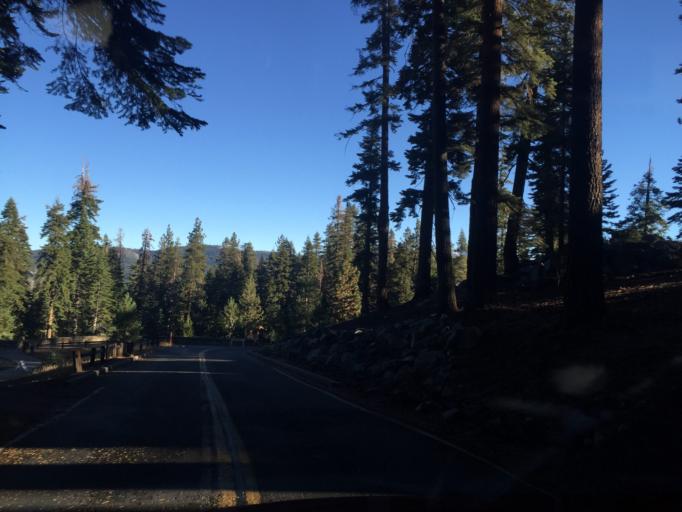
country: US
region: California
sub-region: Mariposa County
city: Yosemite Valley
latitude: 37.7265
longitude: -119.5745
